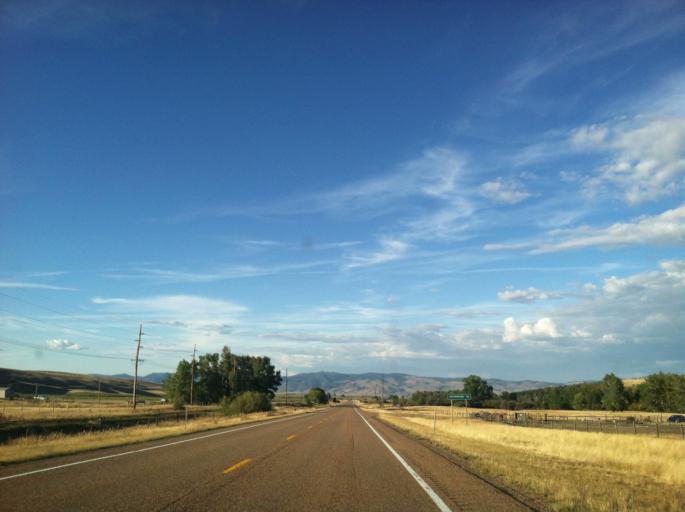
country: US
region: Montana
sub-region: Granite County
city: Philipsburg
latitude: 46.5371
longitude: -113.2217
